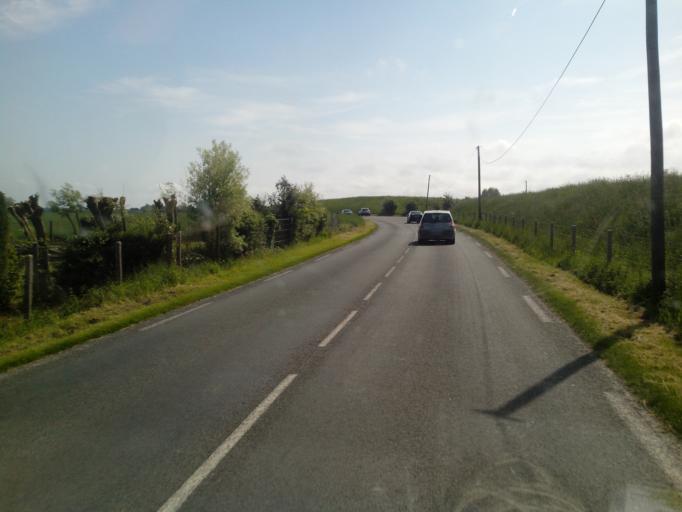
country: FR
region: Picardie
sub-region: Departement de la Somme
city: Quend
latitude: 50.3295
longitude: 1.6425
